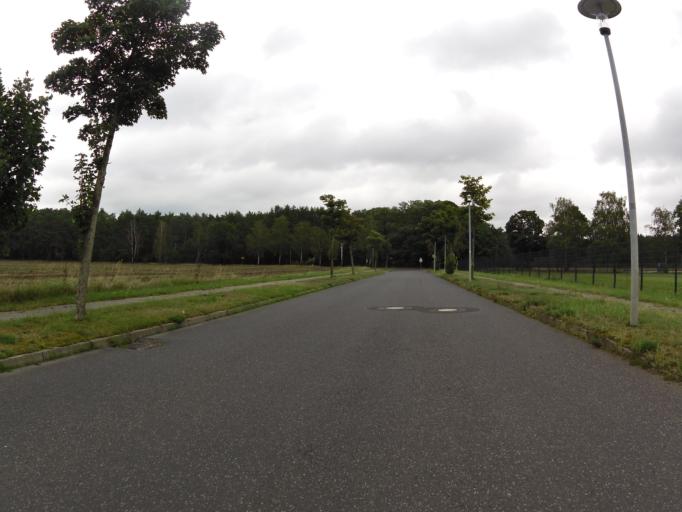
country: DE
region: Brandenburg
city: Storkow
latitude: 52.2713
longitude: 13.9421
